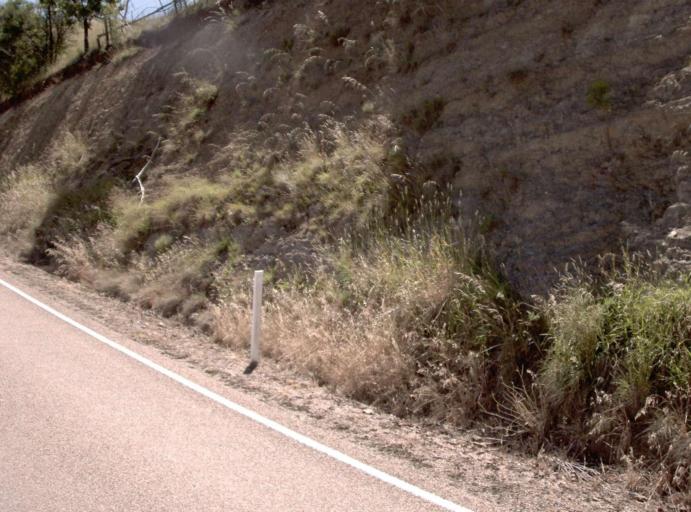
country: AU
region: Victoria
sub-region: East Gippsland
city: Lakes Entrance
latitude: -37.4873
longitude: 148.1869
